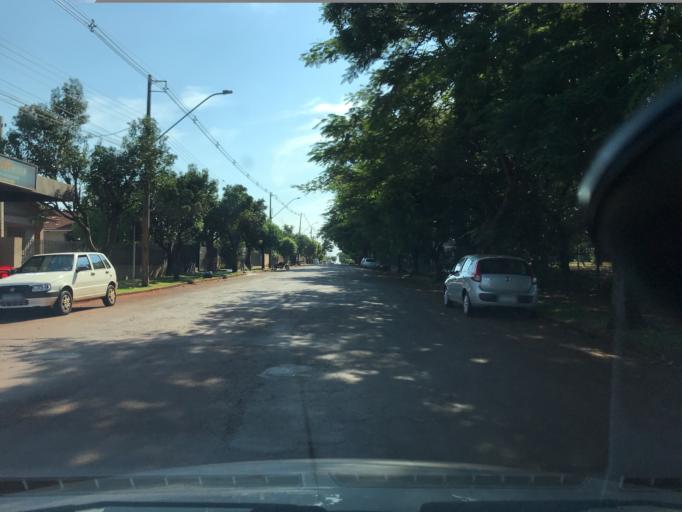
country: BR
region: Parana
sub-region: Palotina
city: Palotina
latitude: -24.2908
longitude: -53.8427
